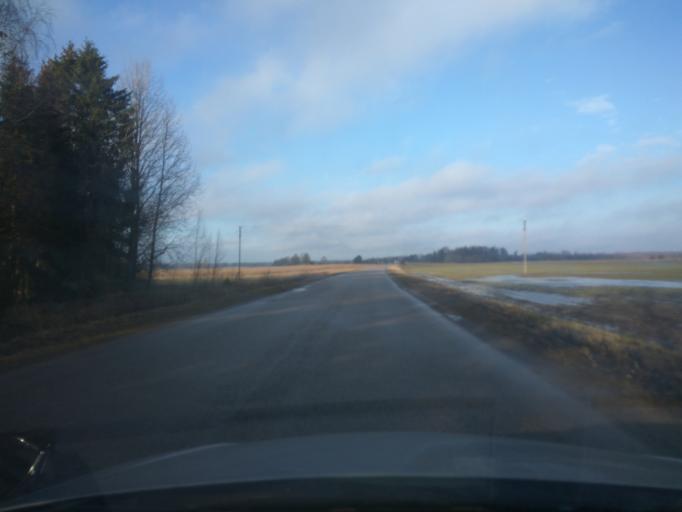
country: LV
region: Saldus Rajons
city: Saldus
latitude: 56.8181
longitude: 22.3785
